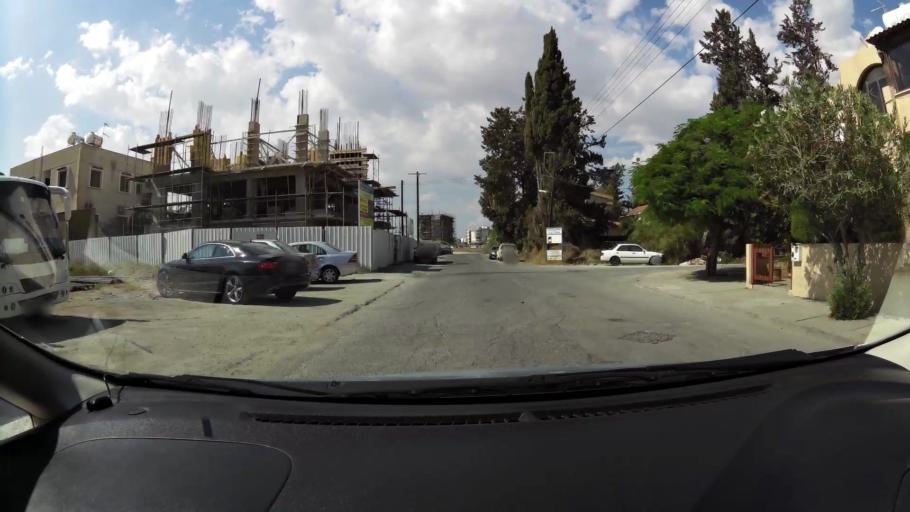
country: CY
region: Larnaka
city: Larnaca
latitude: 34.9098
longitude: 33.6271
